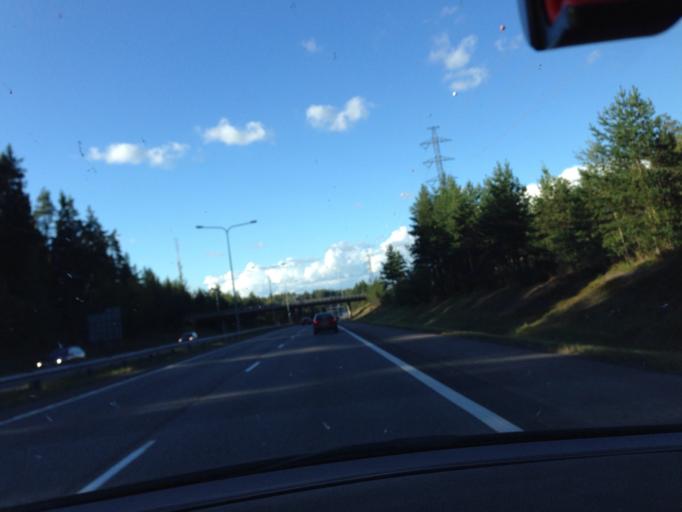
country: FI
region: Uusimaa
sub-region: Helsinki
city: Vantaa
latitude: 60.3157
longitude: 24.9975
